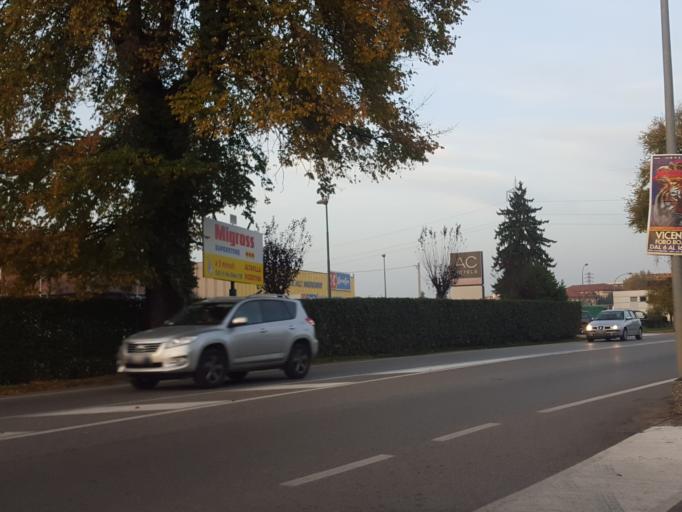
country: IT
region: Veneto
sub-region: Provincia di Vicenza
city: Creazzo
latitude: 45.5313
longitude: 11.5025
